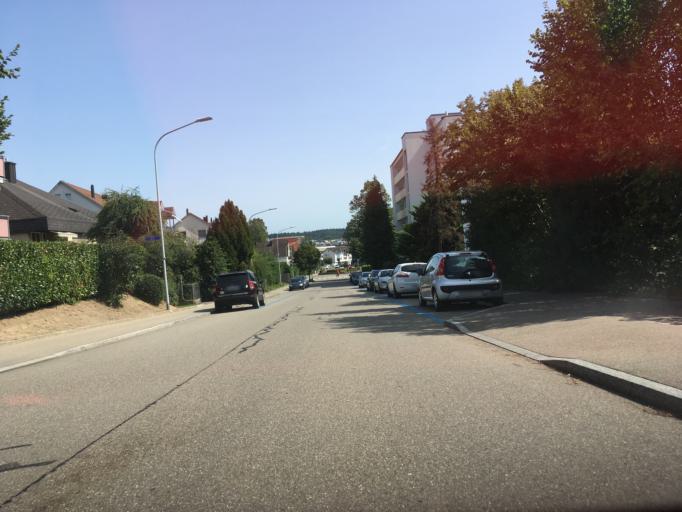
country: CH
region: Zurich
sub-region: Bezirk Buelach
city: Dietlikon / Eichwiesen
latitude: 47.4275
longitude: 8.6171
